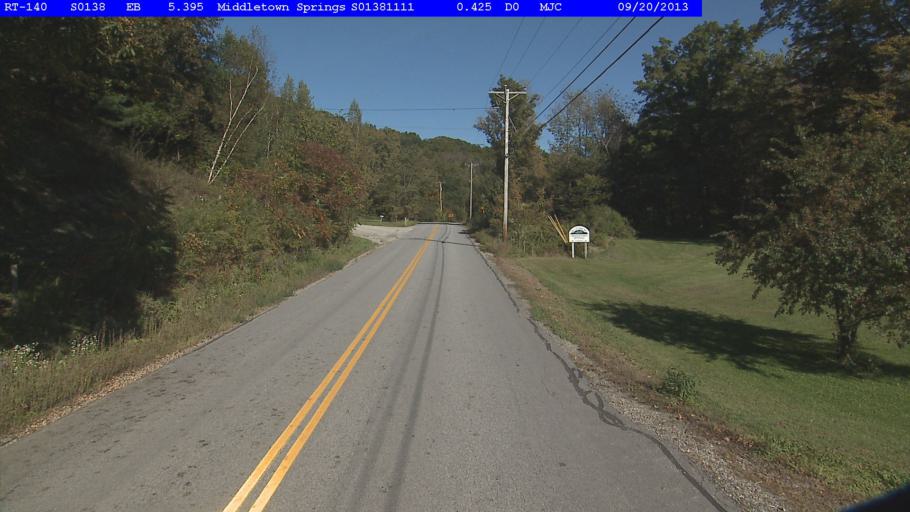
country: US
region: Vermont
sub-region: Rutland County
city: Poultney
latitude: 43.4966
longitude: -73.1630
